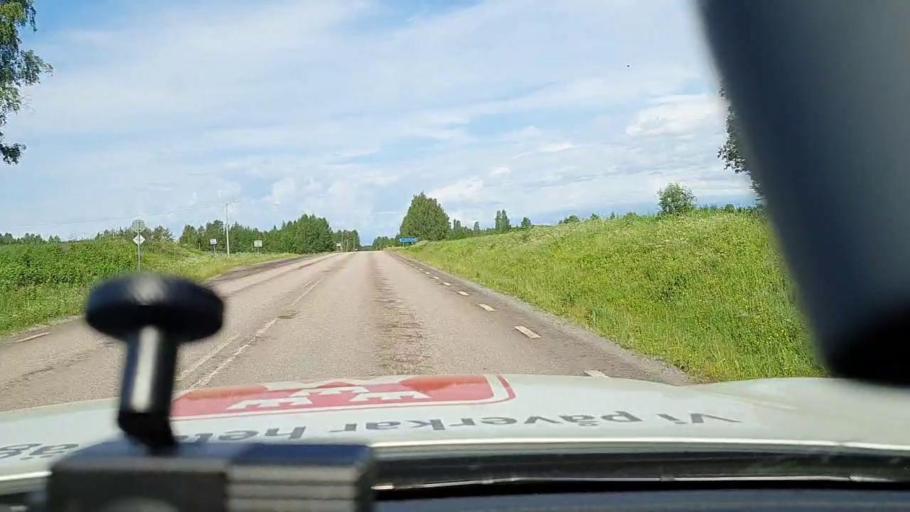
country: SE
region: Norrbotten
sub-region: Alvsbyns Kommun
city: AElvsbyn
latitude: 66.0147
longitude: 21.1632
